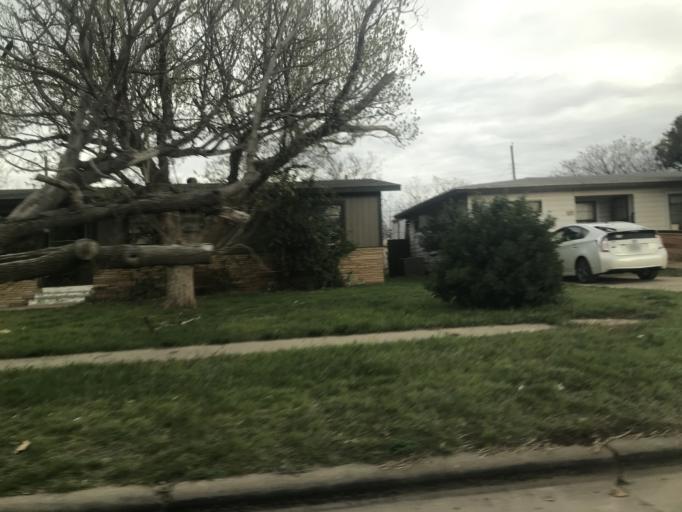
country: US
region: Texas
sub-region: Taylor County
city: Abilene
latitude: 32.4613
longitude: -99.7557
